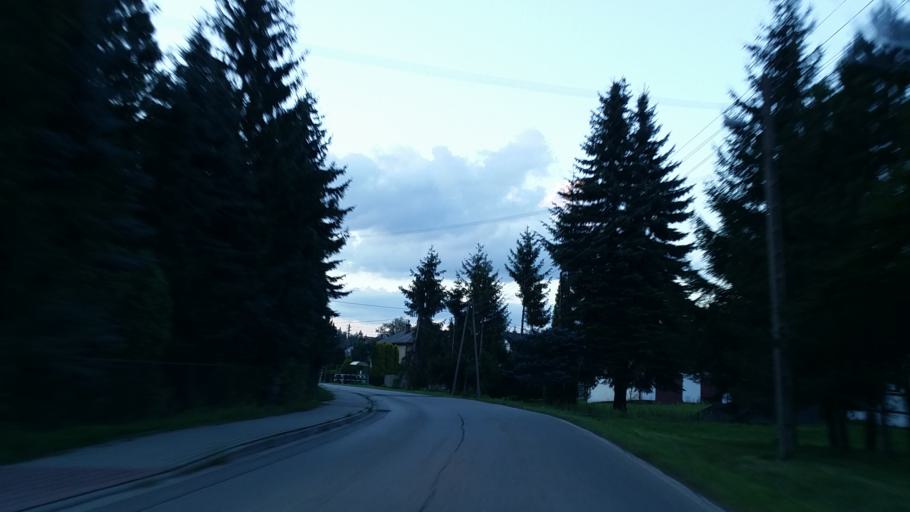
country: PL
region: Lesser Poland Voivodeship
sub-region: Powiat oswiecimski
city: Przeciszow
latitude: 50.0140
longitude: 19.3738
